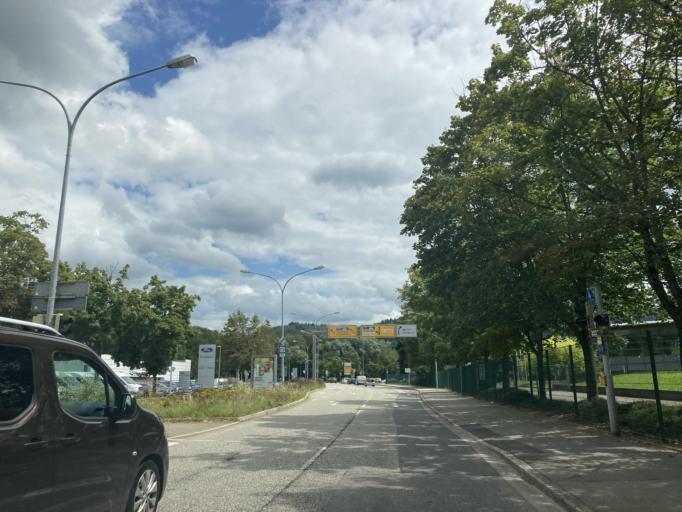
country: DE
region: Baden-Wuerttemberg
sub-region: Freiburg Region
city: Gundelfingen
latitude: 48.0339
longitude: 7.8579
